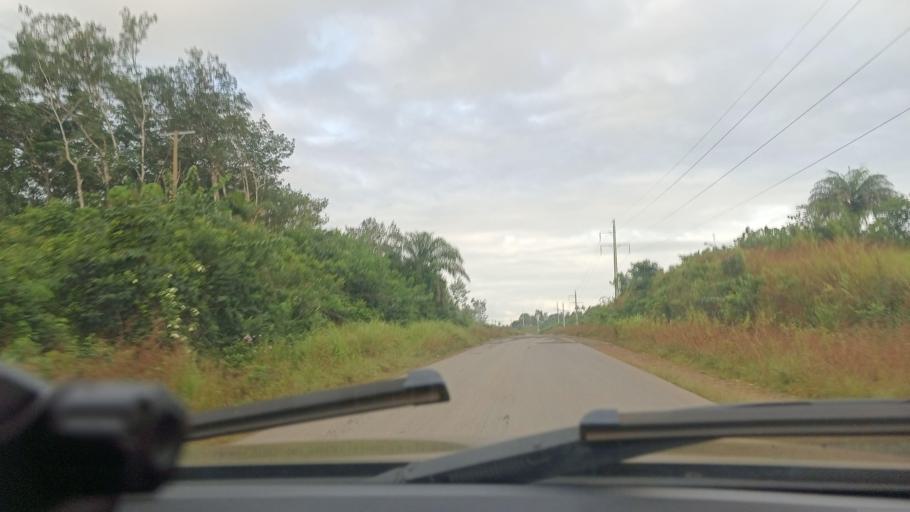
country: LR
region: Montserrado
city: Monrovia
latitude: 6.5557
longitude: -10.8669
